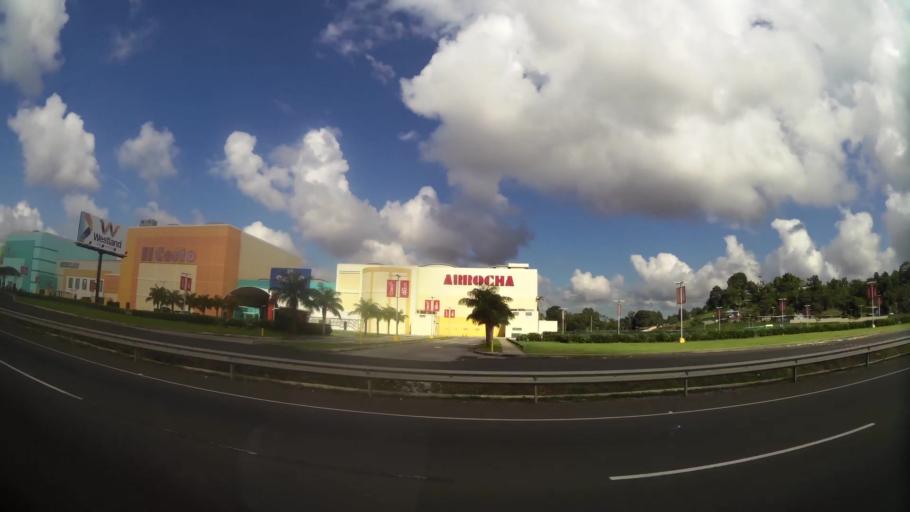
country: PA
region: Panama
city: Vista Alegre
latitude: 8.9215
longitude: -79.7028
